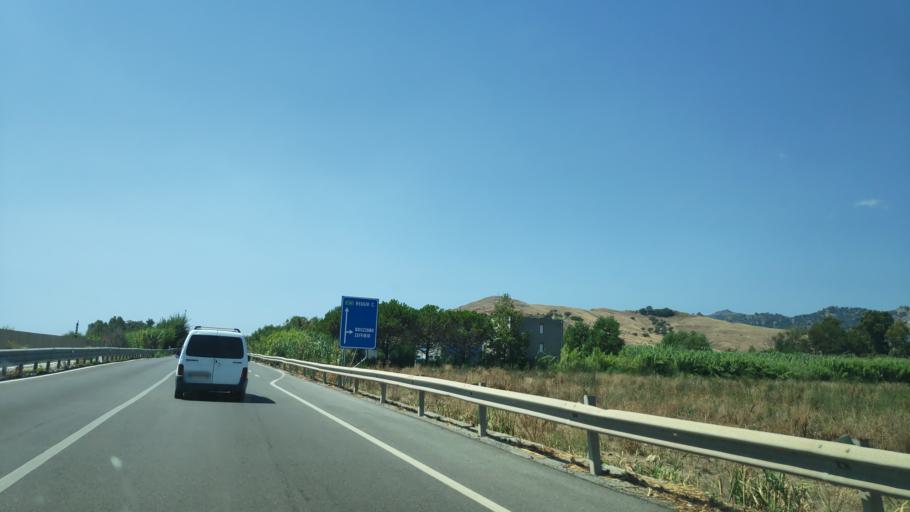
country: IT
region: Calabria
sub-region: Provincia di Reggio Calabria
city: Brancaleone-Marina
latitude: 37.9846
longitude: 16.1166
